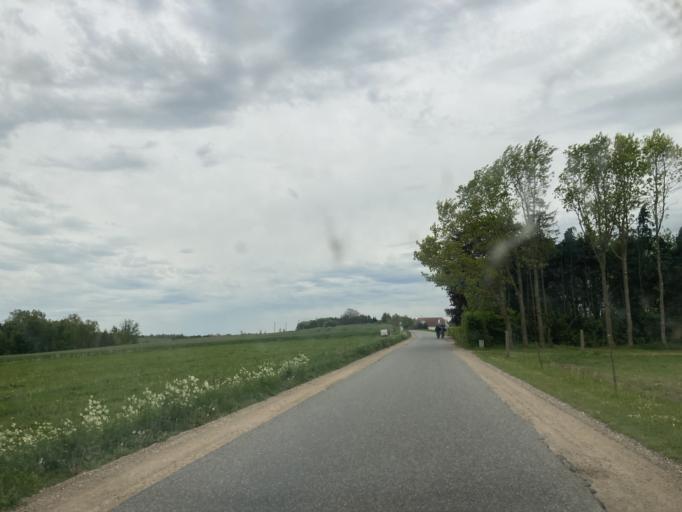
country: DK
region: Zealand
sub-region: Roskilde Kommune
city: Svogerslev
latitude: 55.6501
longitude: 11.9890
